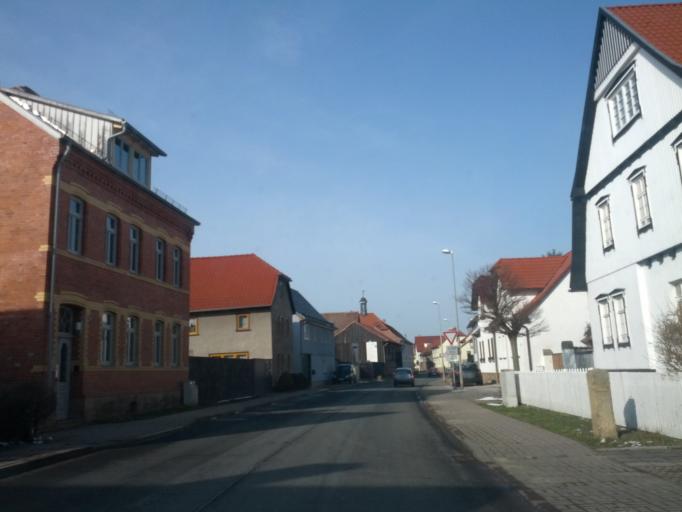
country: DE
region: Thuringia
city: Wandersleben
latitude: 50.8959
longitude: 10.8497
